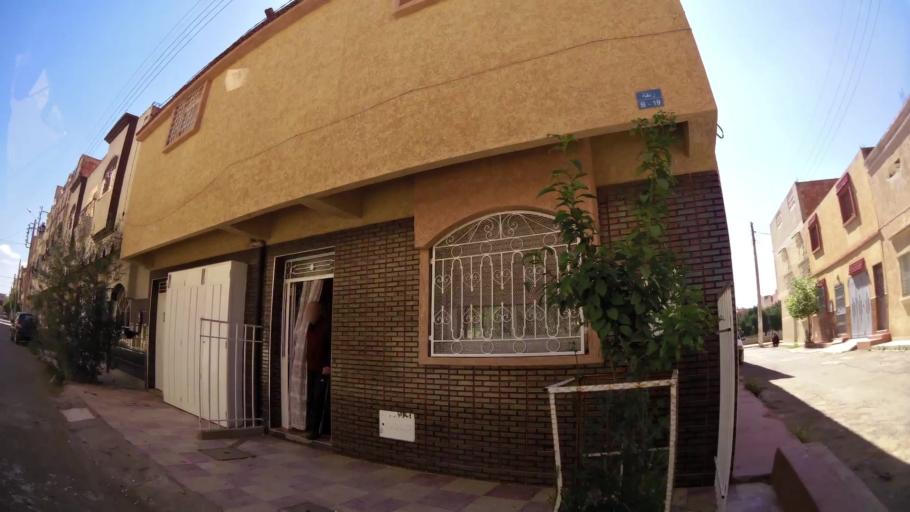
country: MA
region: Oriental
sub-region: Oujda-Angad
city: Oujda
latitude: 34.6603
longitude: -1.9303
